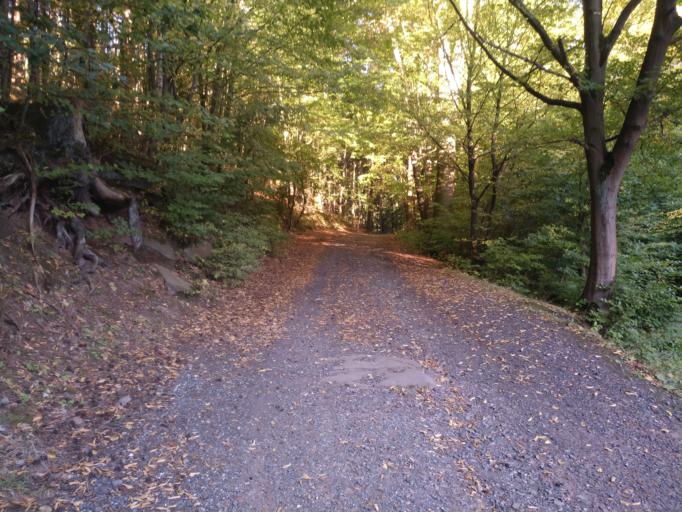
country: DE
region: Thuringia
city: Weissenborn
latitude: 50.9491
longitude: 11.8845
